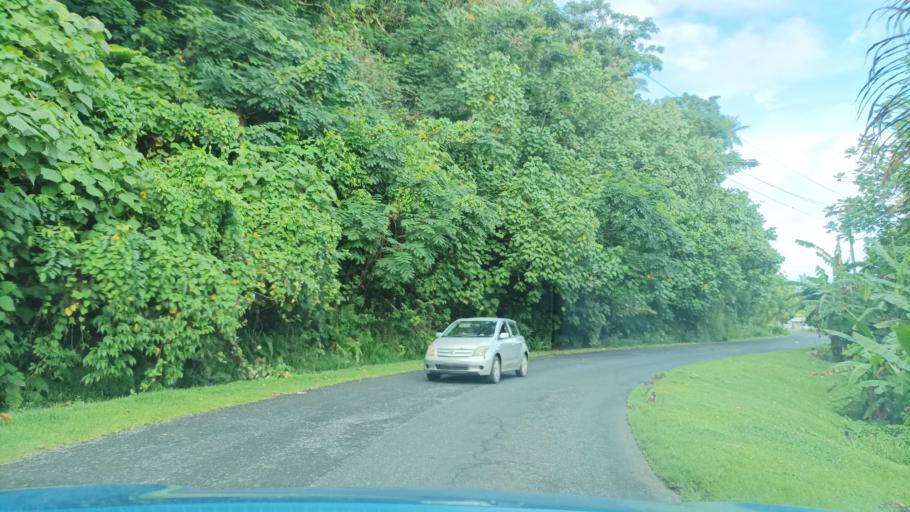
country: FM
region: Pohnpei
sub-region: Kolonia Municipality
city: Kolonia
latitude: 6.9686
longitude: 158.2607
